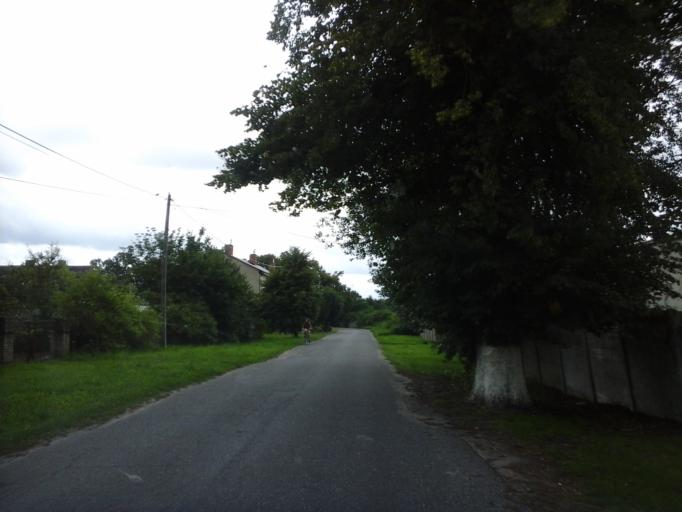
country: PL
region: West Pomeranian Voivodeship
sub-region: Powiat choszczenski
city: Krzecin
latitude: 53.0565
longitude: 15.4785
